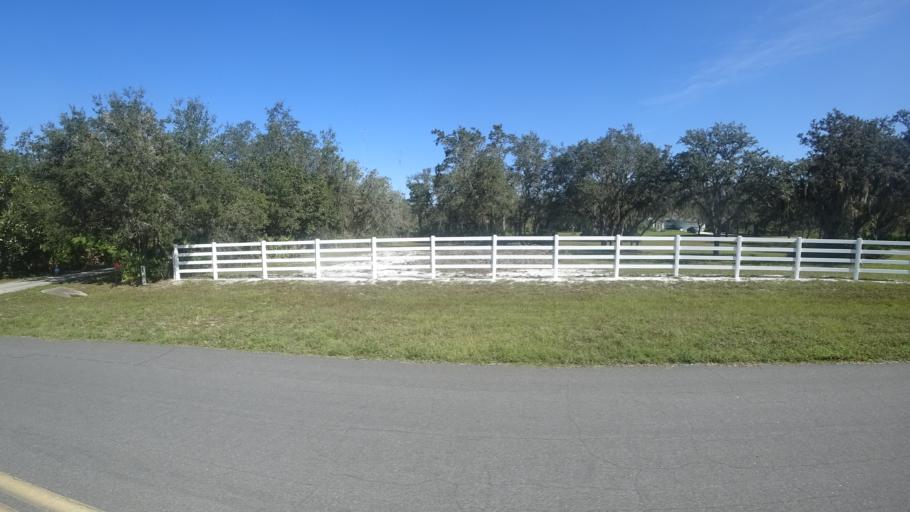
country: US
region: Florida
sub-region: Sarasota County
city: Lake Sarasota
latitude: 27.3591
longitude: -82.2379
